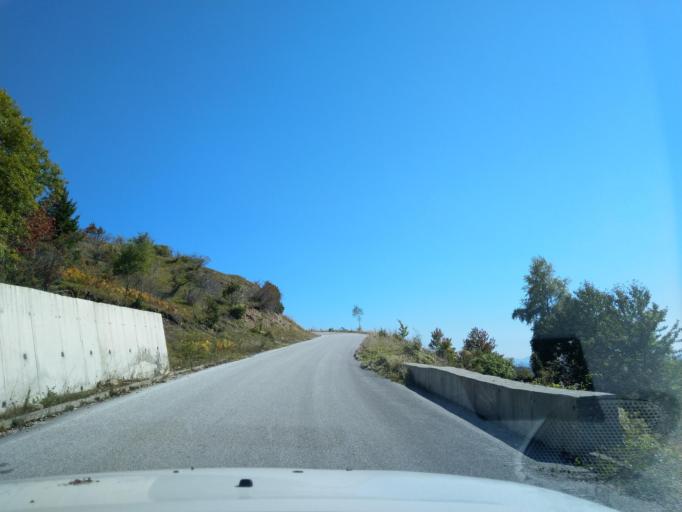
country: RS
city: Sokolovica
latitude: 43.2507
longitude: 20.3268
